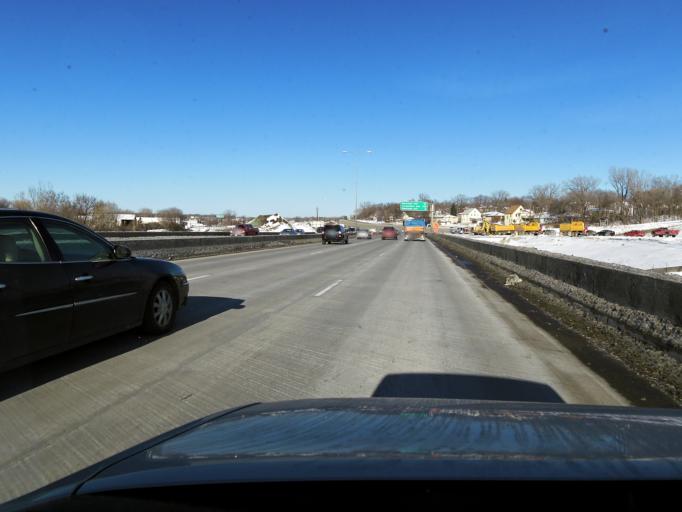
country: US
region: Minnesota
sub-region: Ramsey County
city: Saint Paul
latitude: 44.9688
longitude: -93.0894
